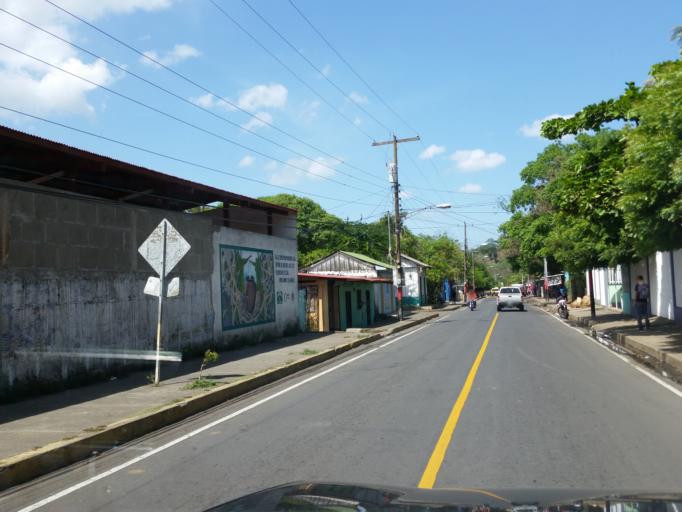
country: NI
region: Masaya
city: La Concepcion
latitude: 11.9529
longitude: -86.1852
